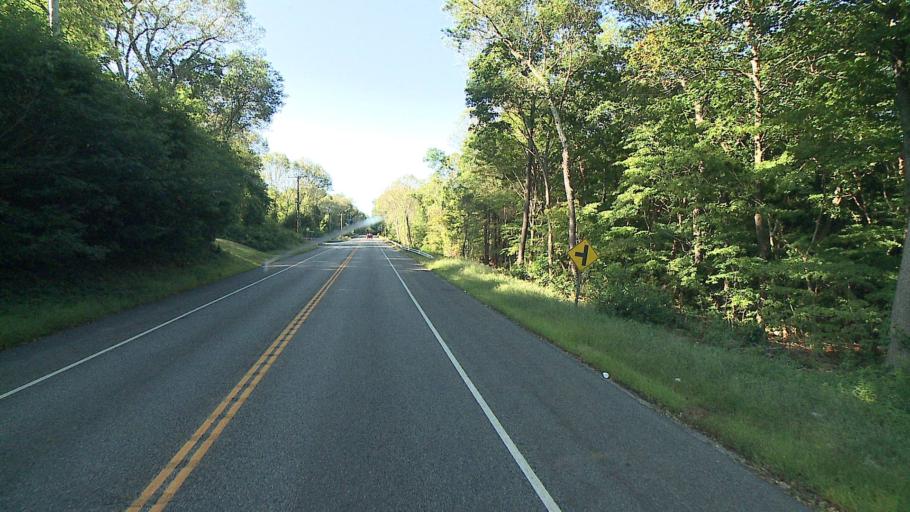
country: US
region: Connecticut
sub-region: New London County
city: Gales Ferry
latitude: 41.4662
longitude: -72.0594
